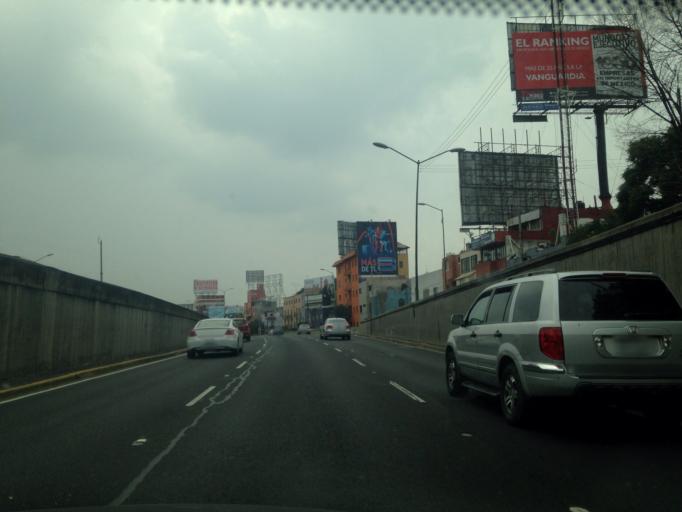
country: MX
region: Mexico City
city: Benito Juarez
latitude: 19.4042
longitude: -99.1559
